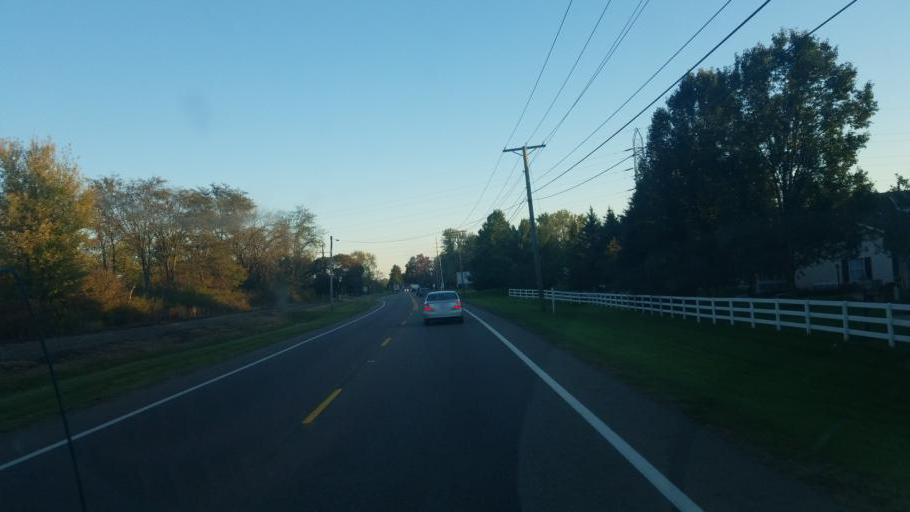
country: US
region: Ohio
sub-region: Licking County
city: Newark
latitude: 40.0940
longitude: -82.4218
